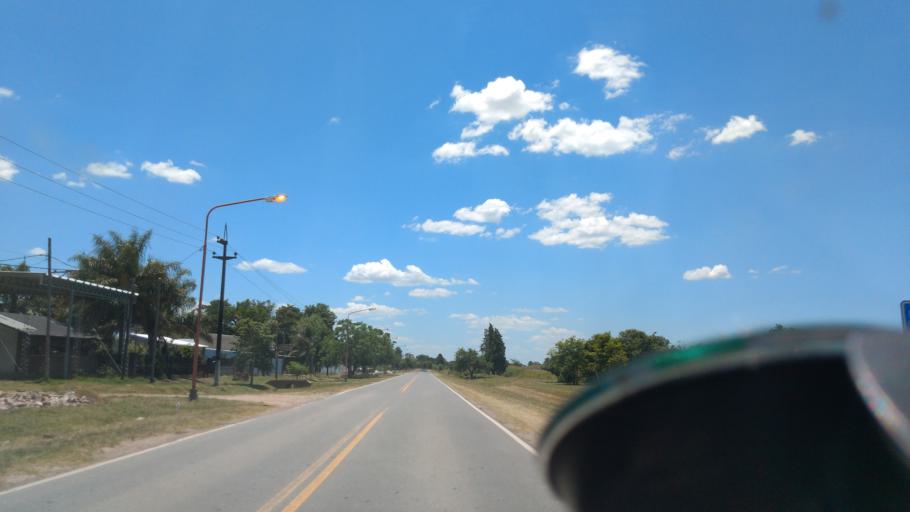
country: AR
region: Santa Fe
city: Laguna Paiva
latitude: -31.3200
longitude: -60.6587
